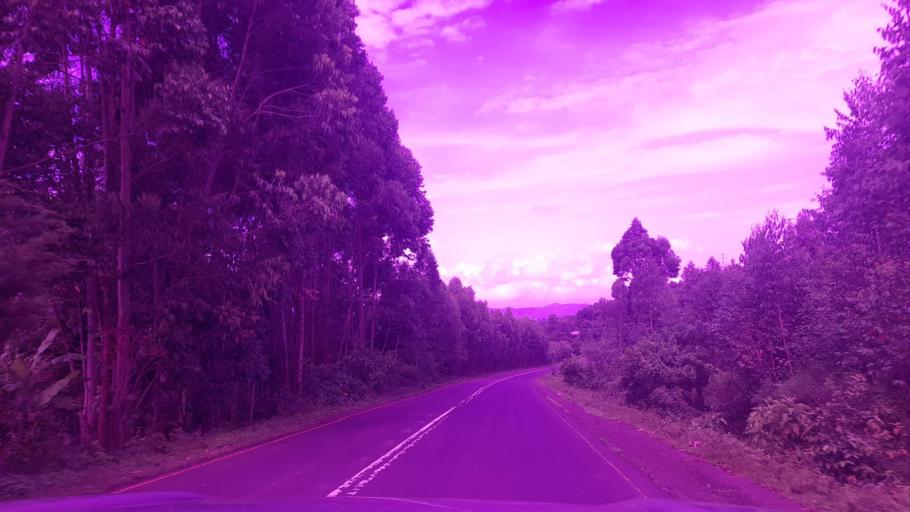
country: ET
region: Oromiya
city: Jima
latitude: 7.5202
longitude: 36.5324
